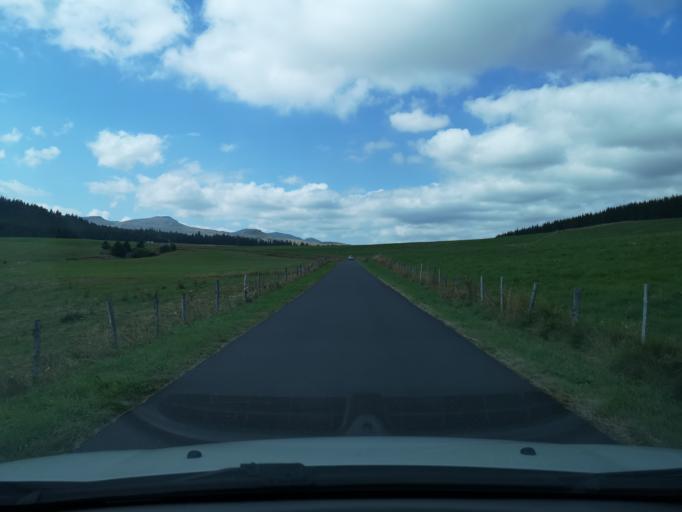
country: FR
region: Auvergne
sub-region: Departement du Puy-de-Dome
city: Mont-Dore
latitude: 45.4845
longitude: 2.9050
